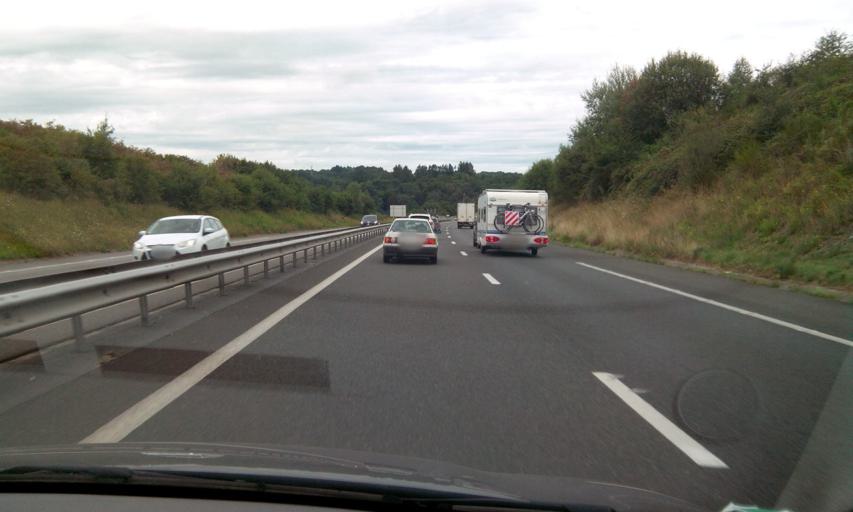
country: FR
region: Limousin
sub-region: Departement de la Correze
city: Uzerche
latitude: 45.4080
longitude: 1.5351
